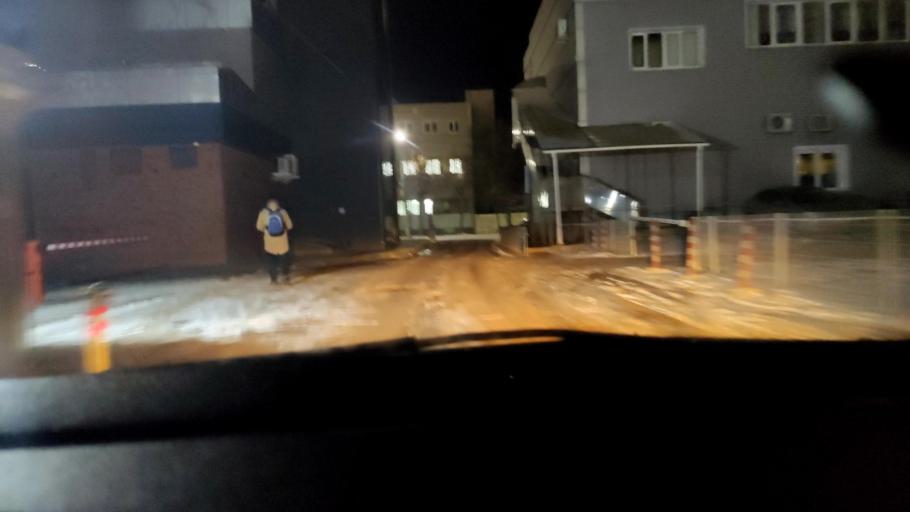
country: RU
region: Voronezj
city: Voronezh
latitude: 51.6803
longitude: 39.1807
